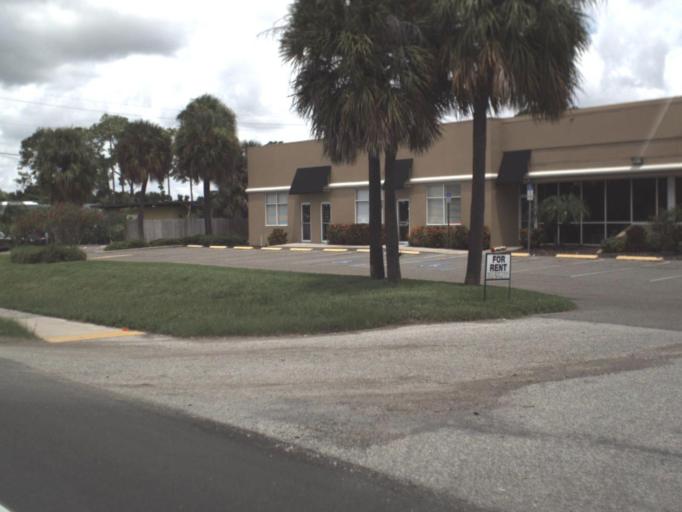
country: US
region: Florida
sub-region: Hillsborough County
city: Egypt Lake-Leto
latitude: 27.9964
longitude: -82.5347
